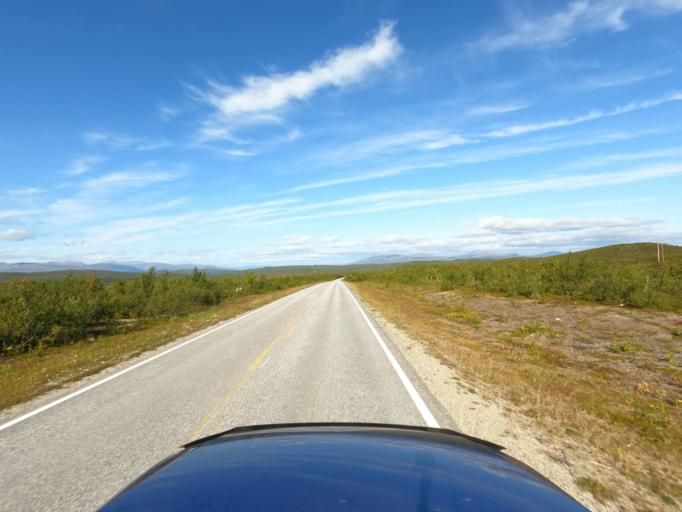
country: NO
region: Finnmark Fylke
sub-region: Karasjok
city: Karasjohka
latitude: 69.7231
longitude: 25.2367
